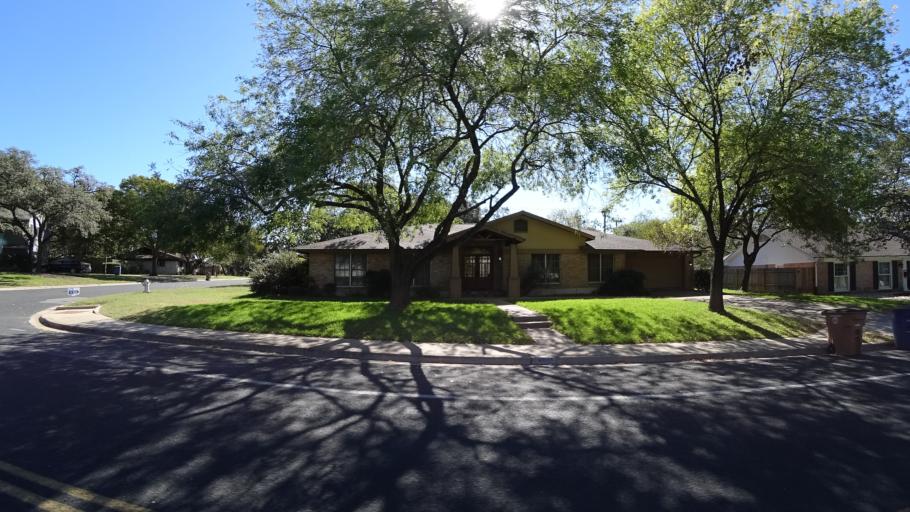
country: US
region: Texas
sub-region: Travis County
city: West Lake Hills
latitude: 30.3554
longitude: -97.7687
